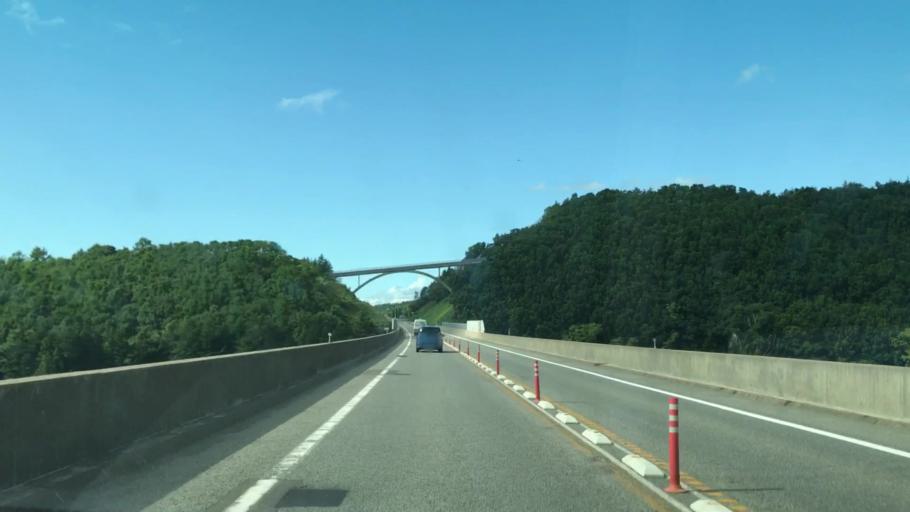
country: JP
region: Hokkaido
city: Date
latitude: 42.4586
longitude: 140.9119
